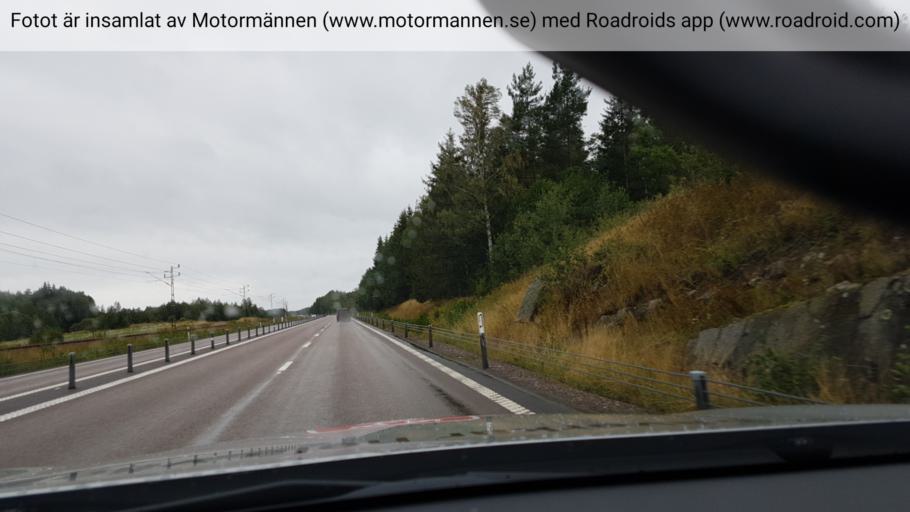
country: SE
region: Vaestra Goetaland
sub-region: Melleruds Kommun
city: Mellerud
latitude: 58.8670
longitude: 12.5632
